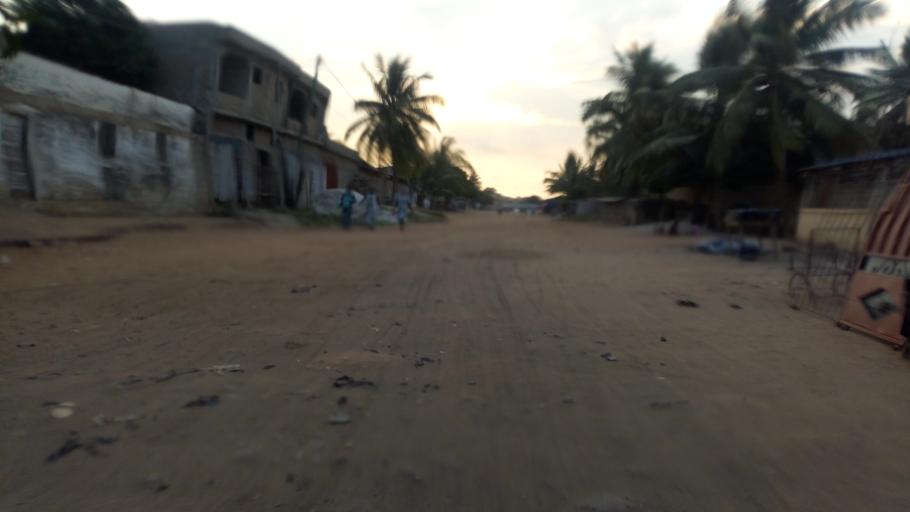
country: TG
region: Maritime
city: Lome
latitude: 6.1902
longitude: 1.1391
